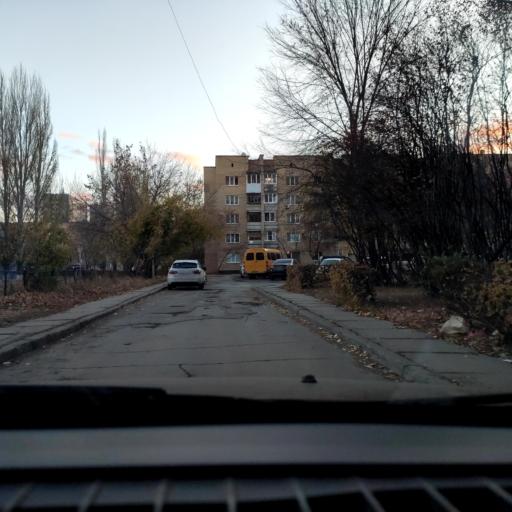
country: RU
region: Samara
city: Tol'yatti
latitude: 53.5155
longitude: 49.2996
